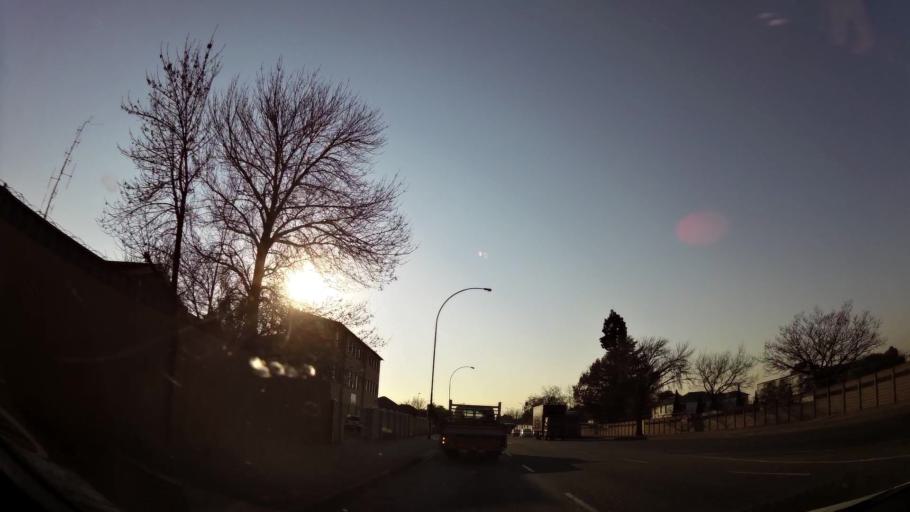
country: ZA
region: Gauteng
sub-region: Ekurhuleni Metropolitan Municipality
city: Germiston
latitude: -26.2228
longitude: 28.1650
